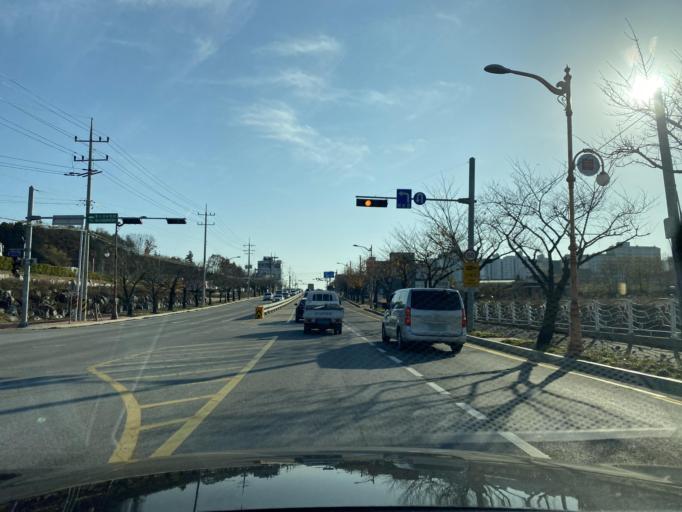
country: KR
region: Chungcheongnam-do
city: Yesan
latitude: 36.7006
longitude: 126.8381
